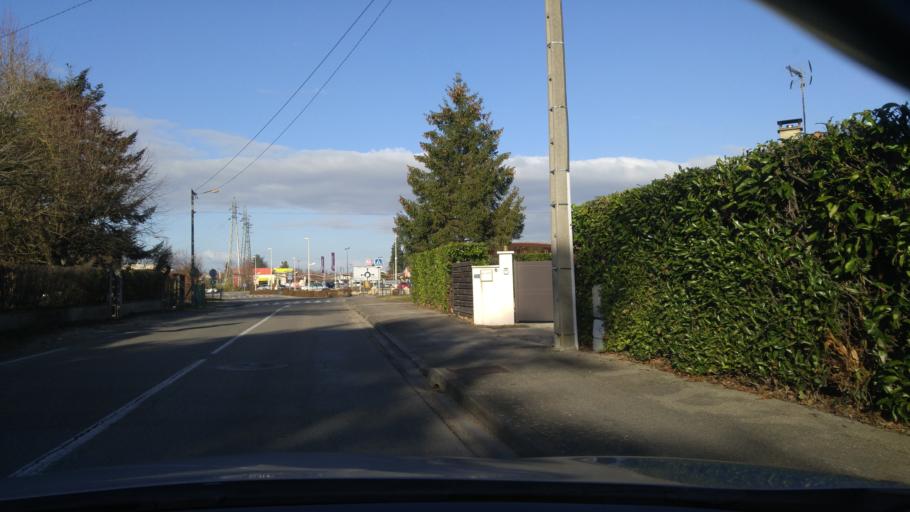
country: FR
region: Rhone-Alpes
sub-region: Departement de l'Isere
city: Pont-de-Cheruy
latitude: 45.7463
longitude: 5.1858
